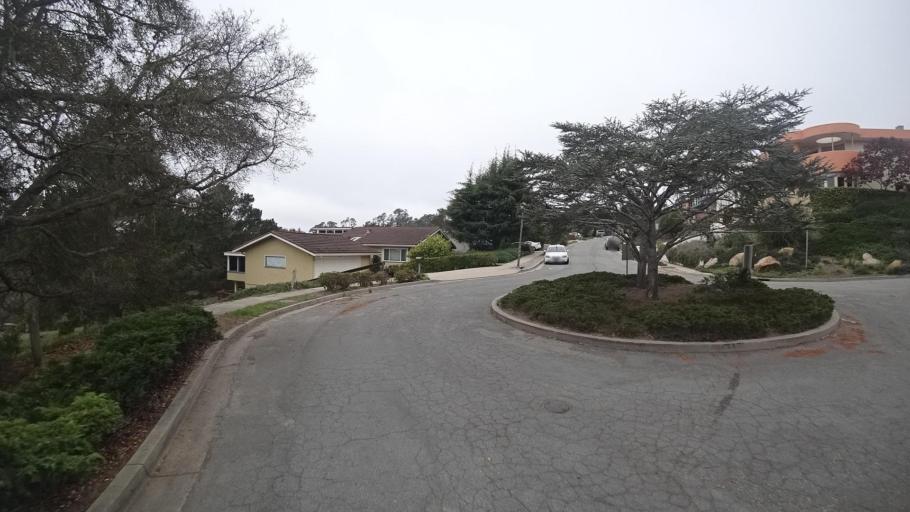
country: US
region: California
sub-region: Monterey County
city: Carmel-by-the-Sea
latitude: 36.5616
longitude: -121.9080
